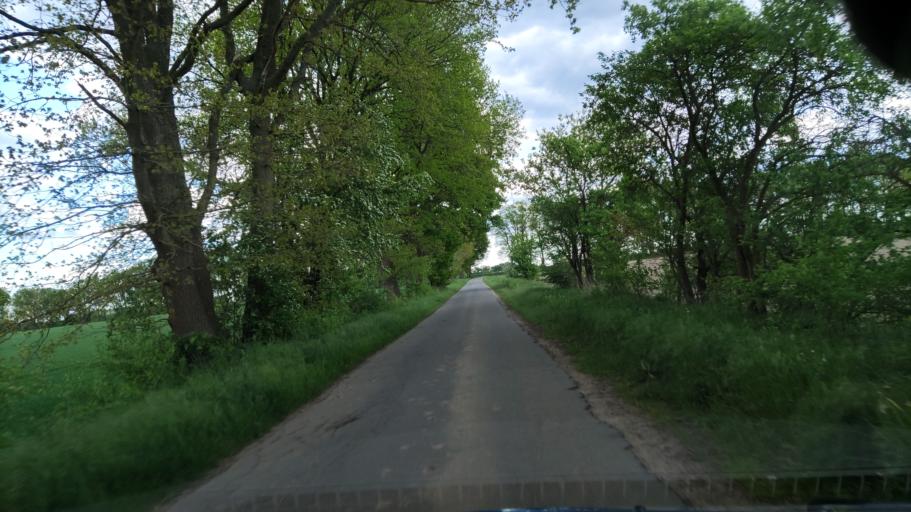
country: DE
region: Lower Saxony
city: Dahlenburg
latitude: 53.1757
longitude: 10.7193
